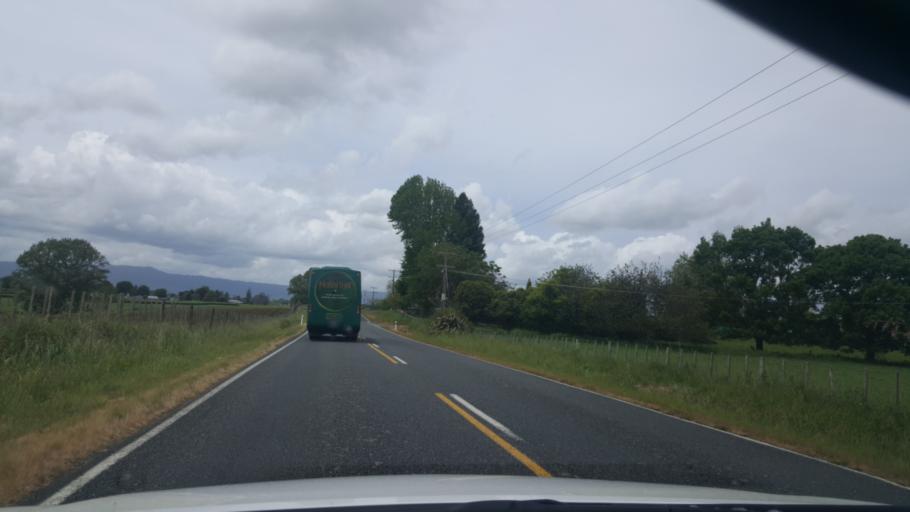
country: NZ
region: Waikato
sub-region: Matamata-Piako District
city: Matamata
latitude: -37.8780
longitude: 175.7104
